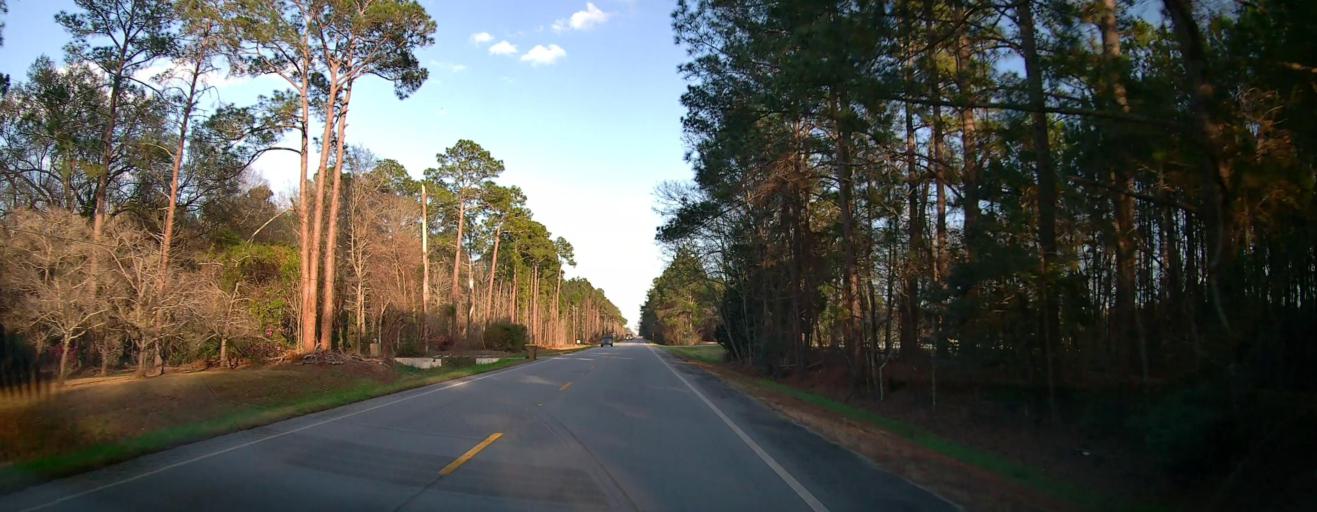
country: US
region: Georgia
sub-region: Bryan County
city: Pembroke
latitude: 32.1379
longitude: -81.6538
